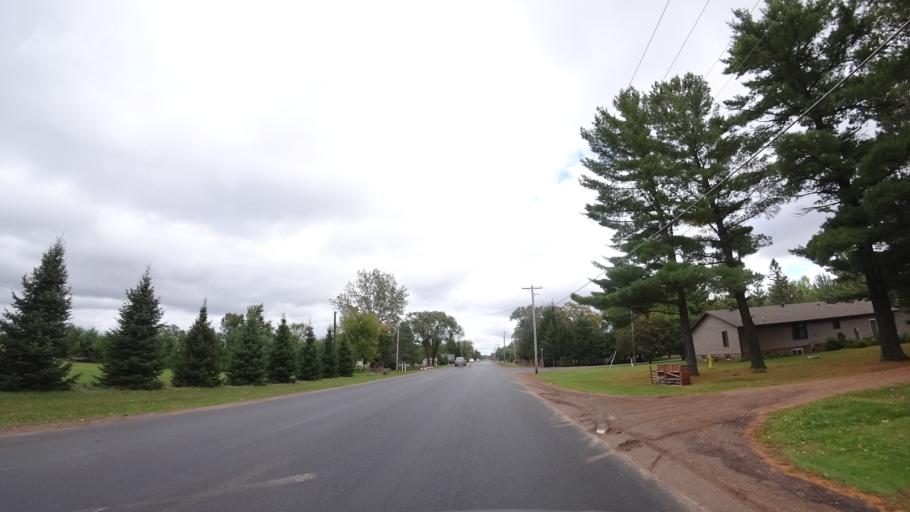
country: US
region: Wisconsin
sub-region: Chippewa County
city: Lake Wissota
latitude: 44.9295
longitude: -91.2788
